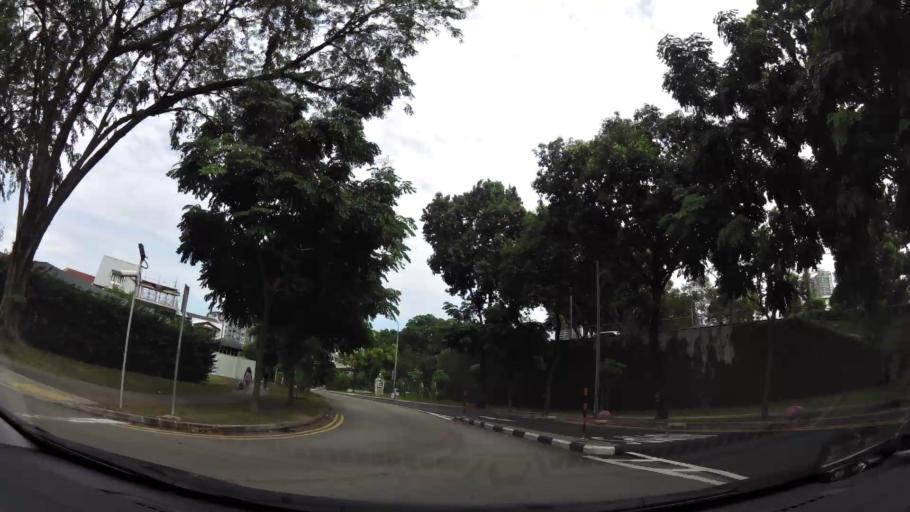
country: SG
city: Singapore
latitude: 1.3125
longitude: 103.7602
